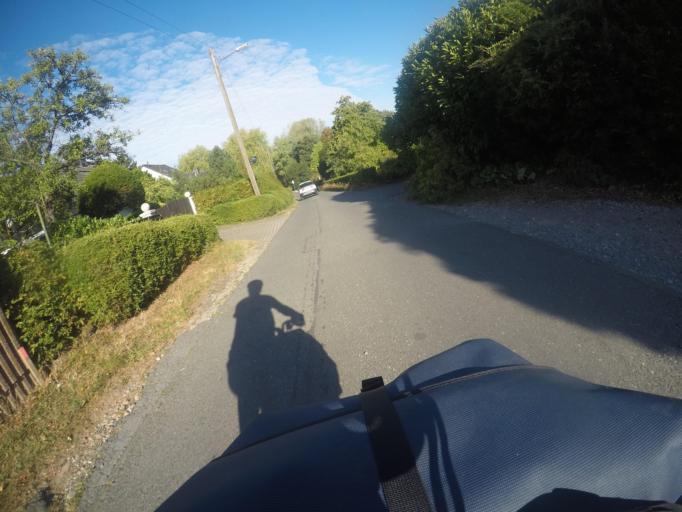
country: DE
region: North Rhine-Westphalia
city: Haan
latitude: 51.2134
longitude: 7.0428
